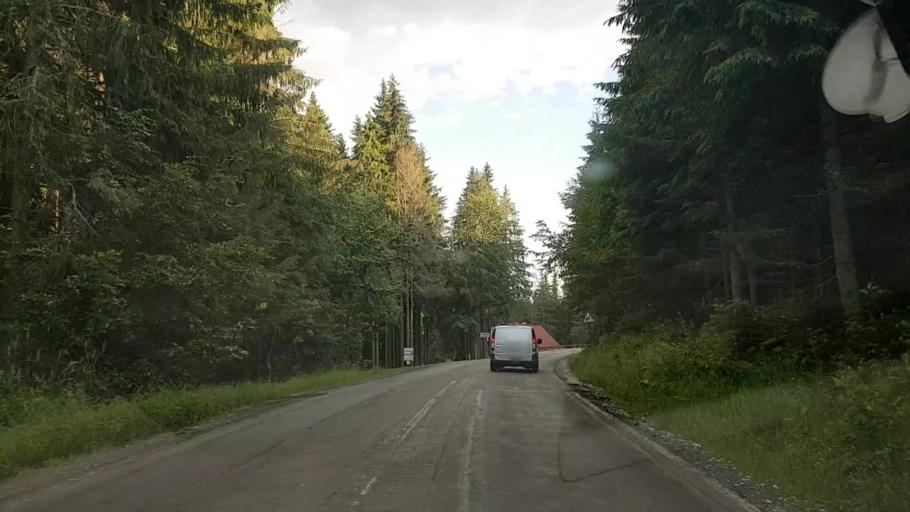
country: RO
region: Harghita
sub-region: Comuna Varsag
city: Varsag
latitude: 46.6631
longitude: 25.3041
